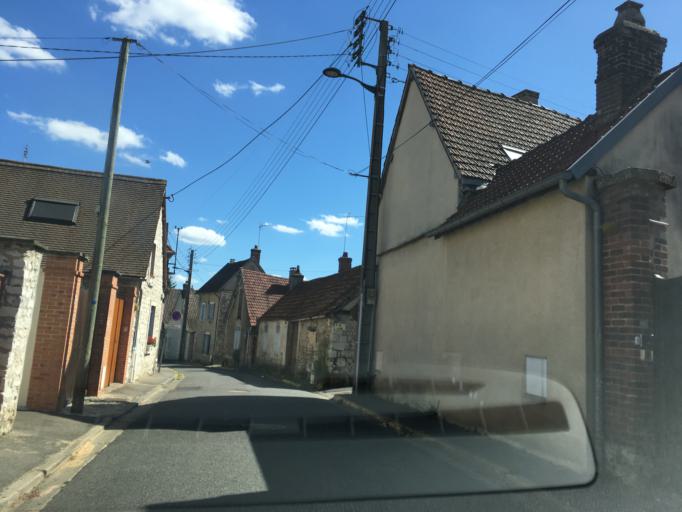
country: FR
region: Haute-Normandie
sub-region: Departement de l'Eure
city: Vernon
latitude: 49.0853
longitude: 1.4929
